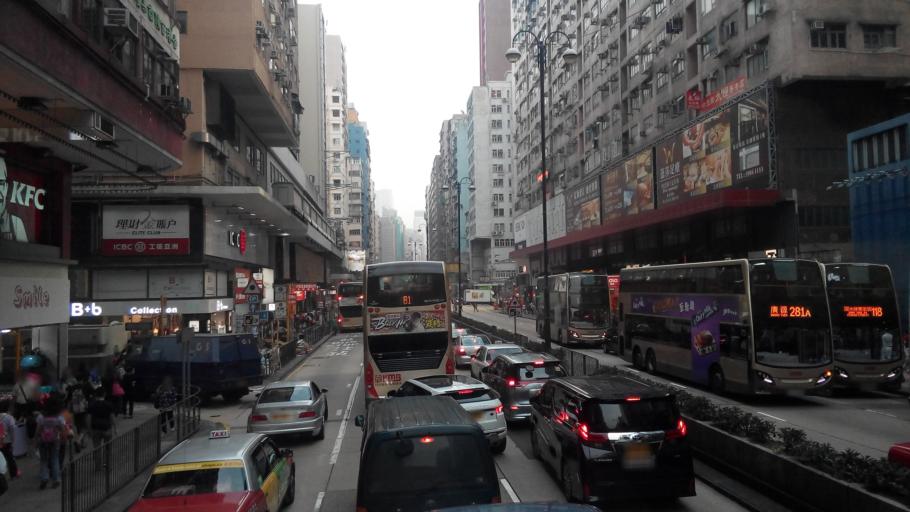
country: HK
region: Kowloon City
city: Kowloon
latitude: 22.3141
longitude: 114.1703
